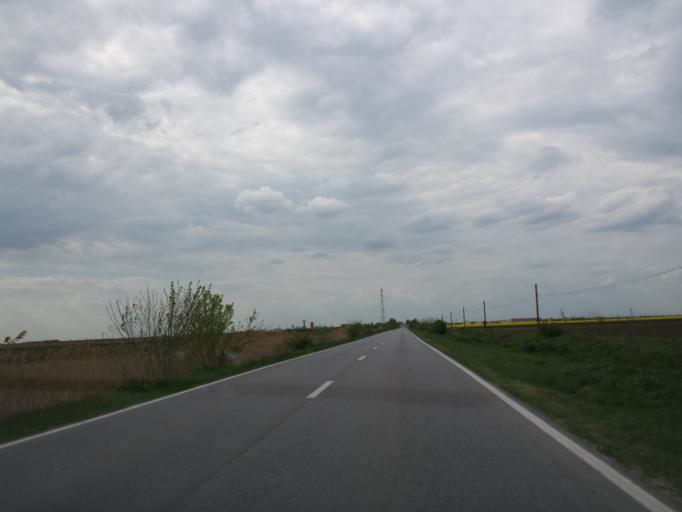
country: RO
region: Timis
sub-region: Comuna Sanpetru Mare
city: Sanpetru Mare
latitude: 46.0404
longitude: 20.6540
